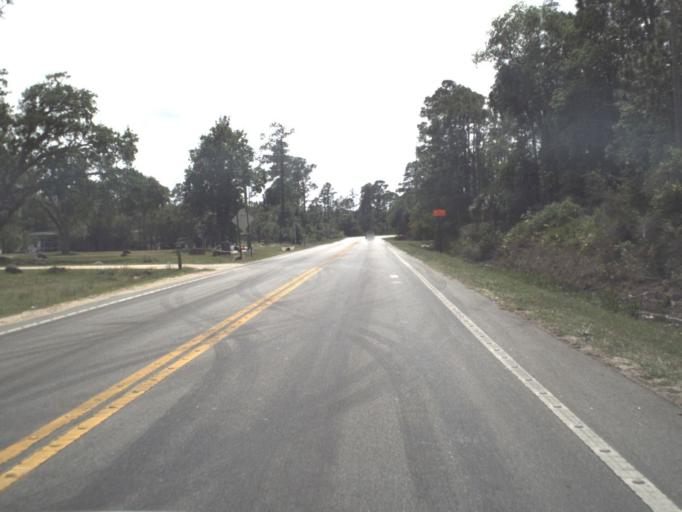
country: US
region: Florida
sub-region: Flagler County
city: Bunnell
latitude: 29.4697
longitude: -81.2727
